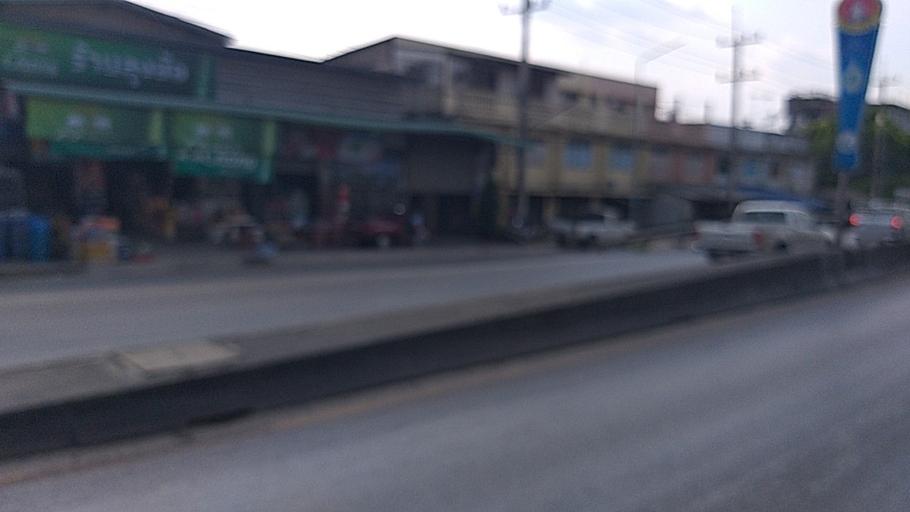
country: TH
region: Pathum Thani
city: Sam Khok
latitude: 14.0680
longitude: 100.5232
